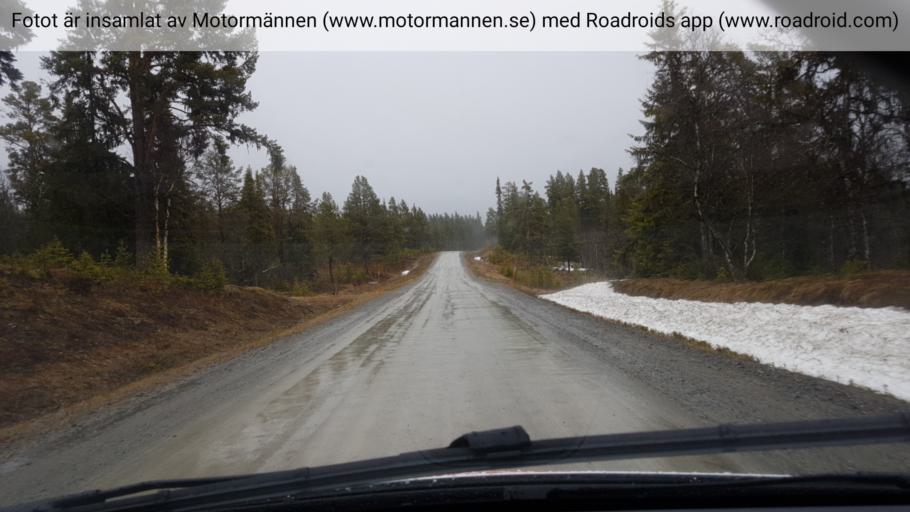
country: SE
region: Jaemtland
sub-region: Are Kommun
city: Are
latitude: 62.6653
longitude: 12.9364
